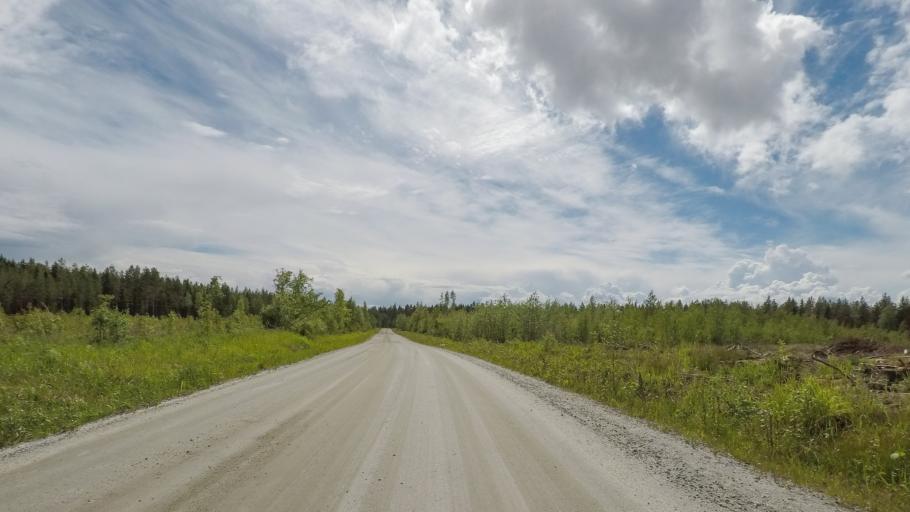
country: FI
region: Central Finland
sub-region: Jyvaeskylae
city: Hankasalmi
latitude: 62.4086
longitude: 26.6043
